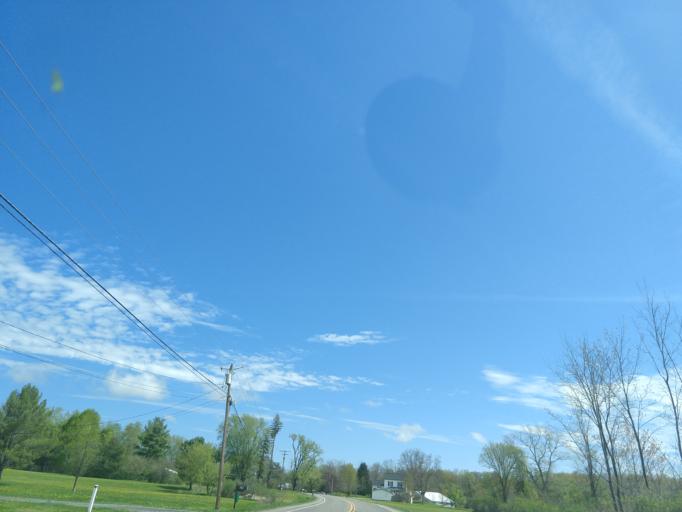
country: US
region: New York
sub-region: Tompkins County
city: Dryden
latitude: 42.5019
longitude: -76.3623
